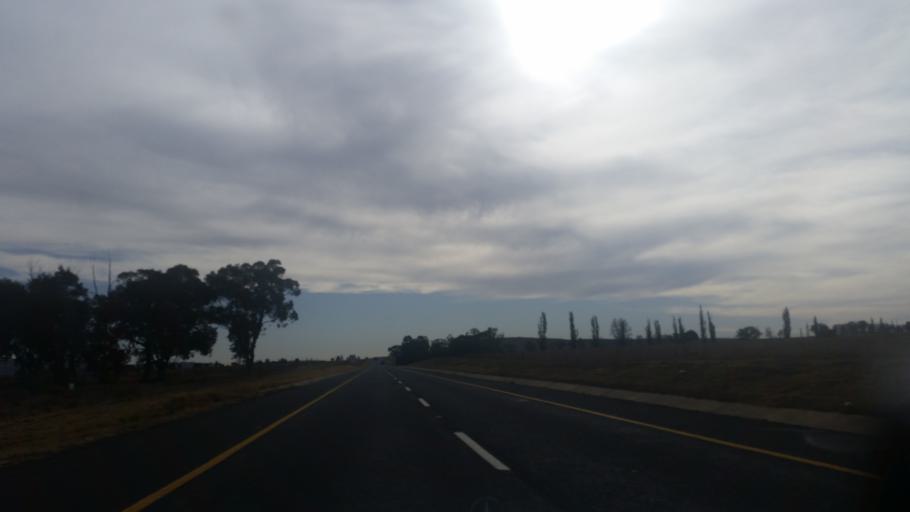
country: ZA
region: Orange Free State
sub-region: Thabo Mofutsanyana District Municipality
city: Phuthaditjhaba
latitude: -28.3124
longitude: 28.7560
